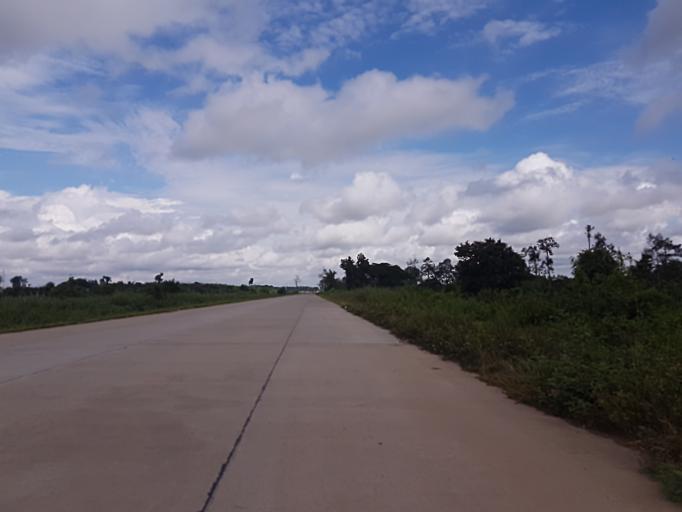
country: TH
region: Nong Khai
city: Nong Khai
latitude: 17.9047
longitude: 102.7099
